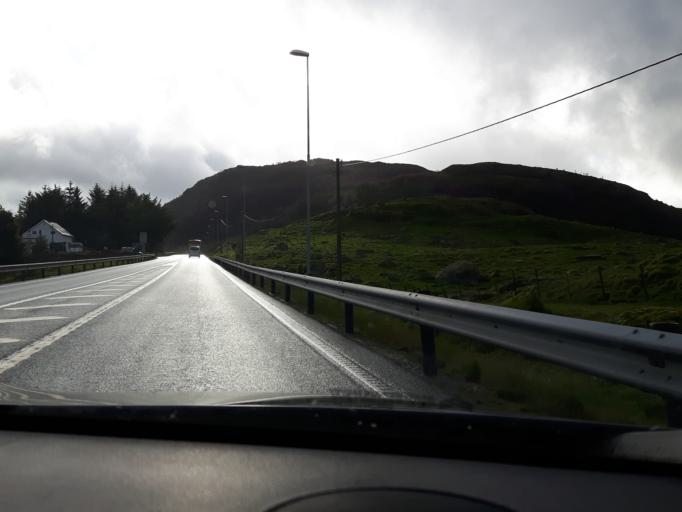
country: NO
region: Rogaland
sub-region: Bjerkreim
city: Vikesa
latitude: 58.6659
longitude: 5.9896
